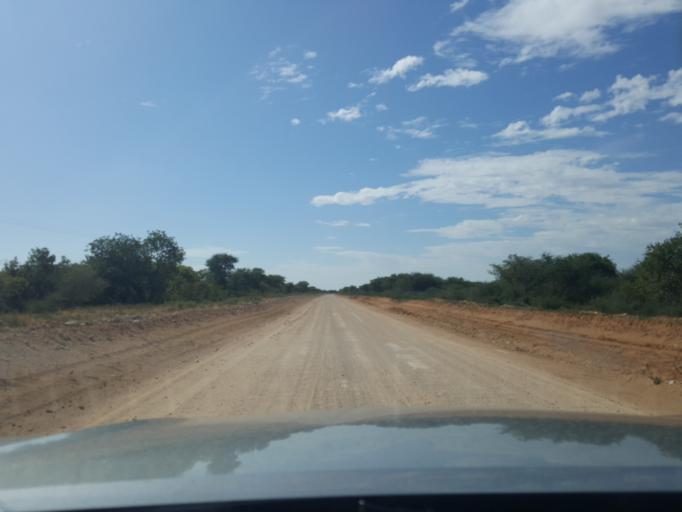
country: BW
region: Kweneng
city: Khudumelapye
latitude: -23.7677
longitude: 24.7648
